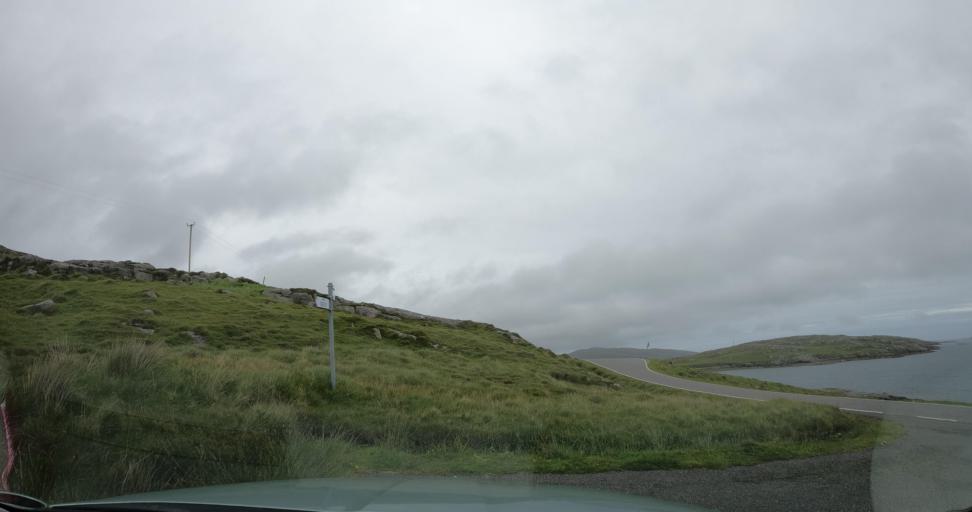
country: GB
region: Scotland
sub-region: Eilean Siar
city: Barra
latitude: 56.9316
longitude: -7.5232
